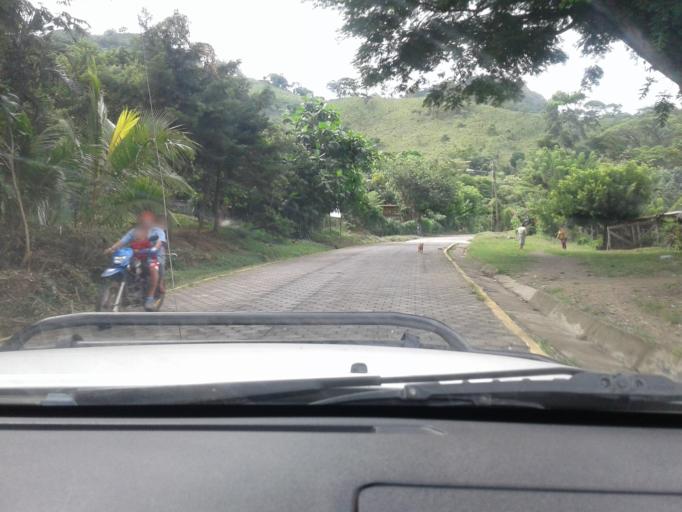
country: NI
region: Matagalpa
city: San Ramon
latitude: 12.9161
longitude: -85.8117
